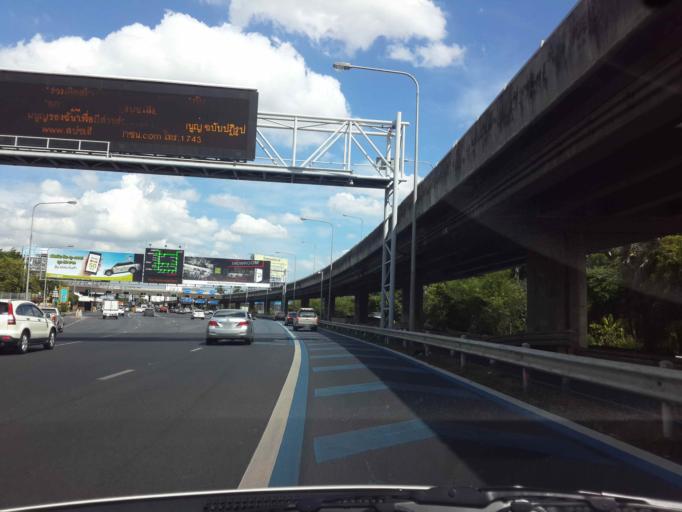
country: TH
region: Bangkok
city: Chom Thong
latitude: 13.6766
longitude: 100.4794
